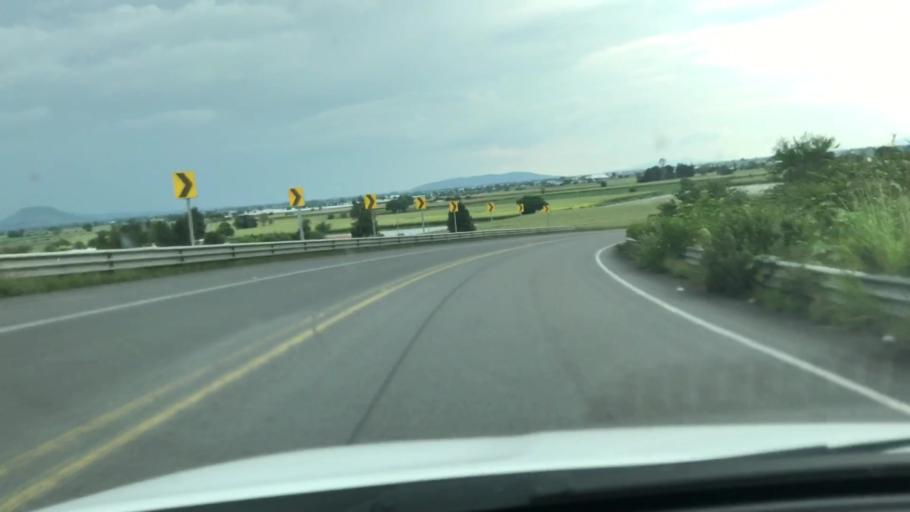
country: MX
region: Michoacan
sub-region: Yurecuaro
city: Yurecuaro
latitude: 20.3274
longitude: -102.2499
